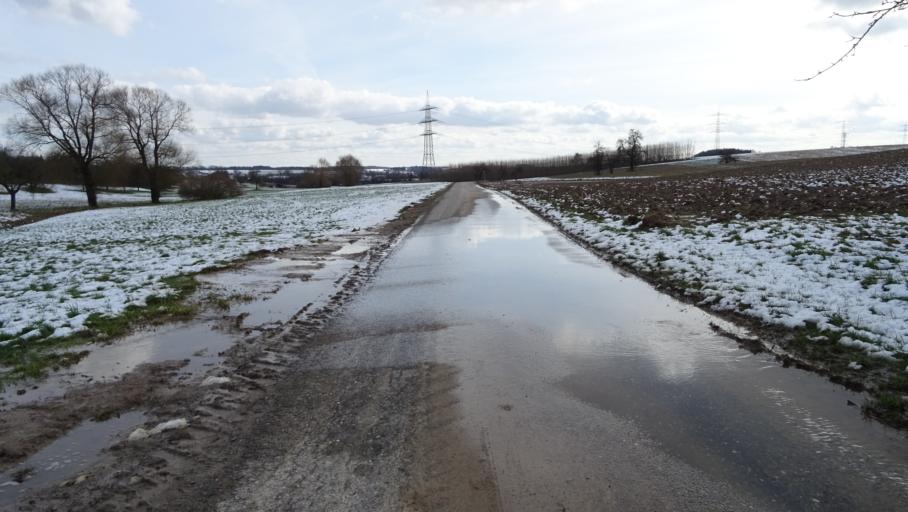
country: DE
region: Baden-Wuerttemberg
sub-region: Karlsruhe Region
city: Seckach
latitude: 49.4244
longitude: 9.2699
